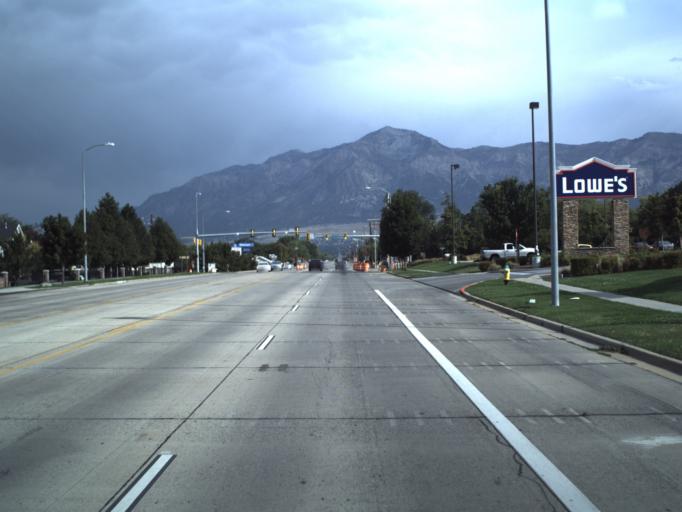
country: US
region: Utah
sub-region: Weber County
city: Harrisville
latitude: 41.2651
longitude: -111.9695
